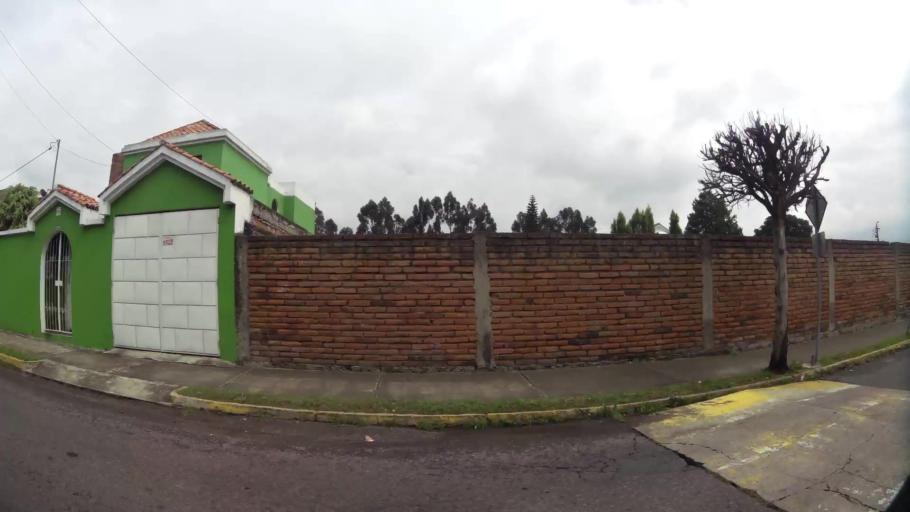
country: EC
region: Pichincha
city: Sangolqui
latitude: -0.3077
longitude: -78.4710
